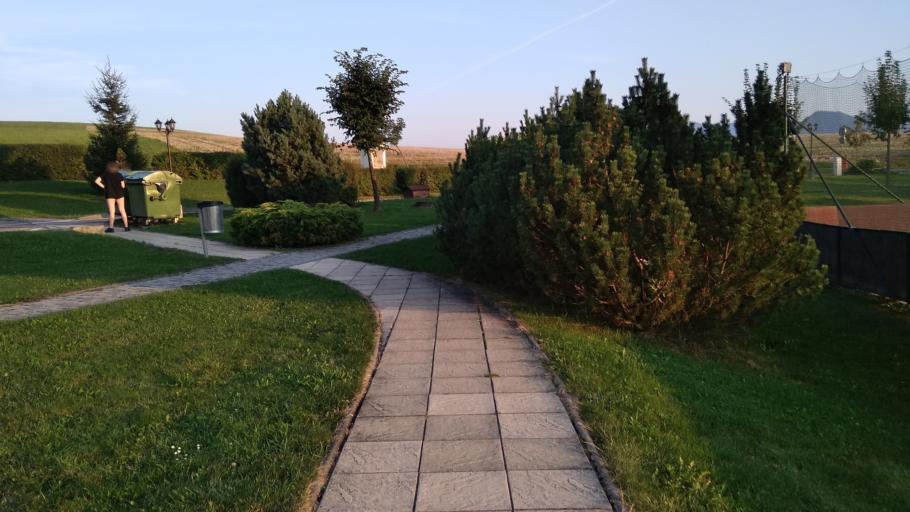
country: SK
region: Zilinsky
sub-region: Okres Liptovsky Mikulas
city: Liptovsky Mikulas
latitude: 49.1075
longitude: 19.5749
